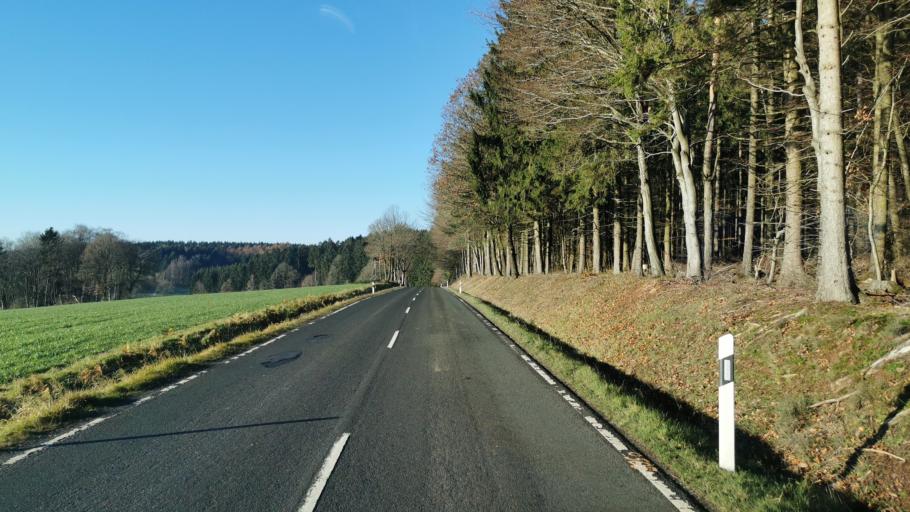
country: DE
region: Rheinland-Pfalz
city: Meisburg
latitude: 50.1148
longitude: 6.6883
